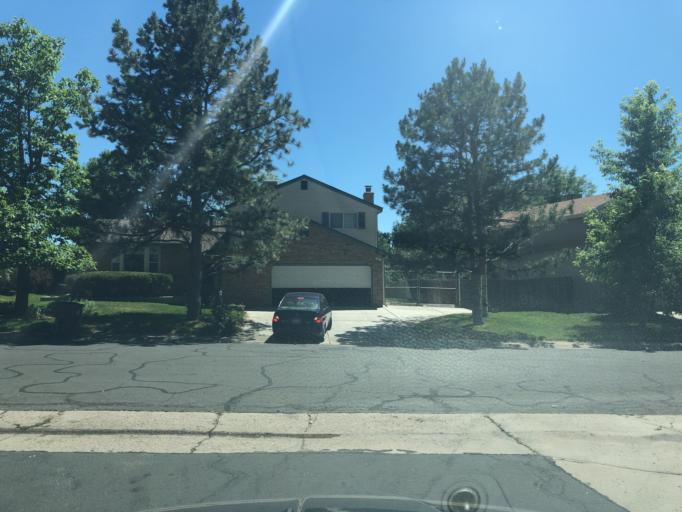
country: US
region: Colorado
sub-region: Arapahoe County
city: Dove Valley
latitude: 39.6180
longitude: -104.7859
